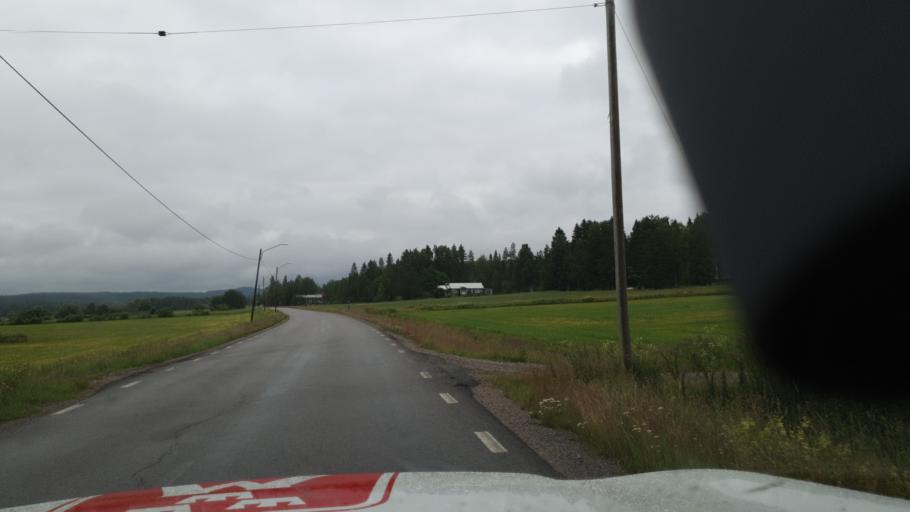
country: SE
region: Vaesterbotten
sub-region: Vannas Kommun
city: Vannasby
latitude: 63.7838
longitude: 19.8653
